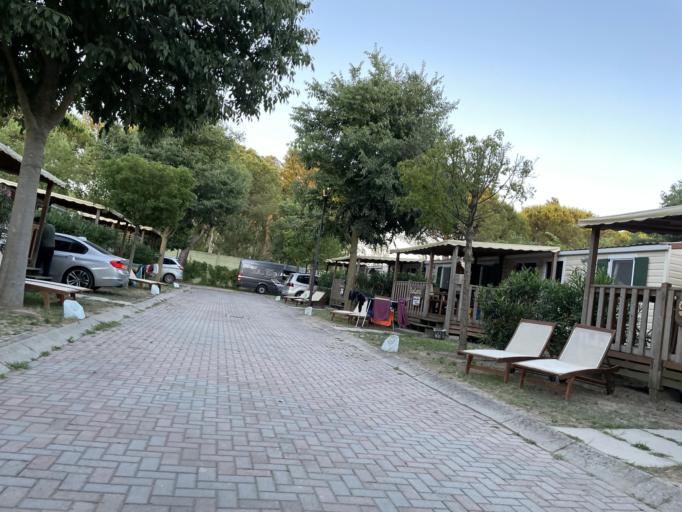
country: IT
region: Emilia-Romagna
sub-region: Provincia di Ferrara
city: San Giuseppe
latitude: 44.7319
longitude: 12.2309
